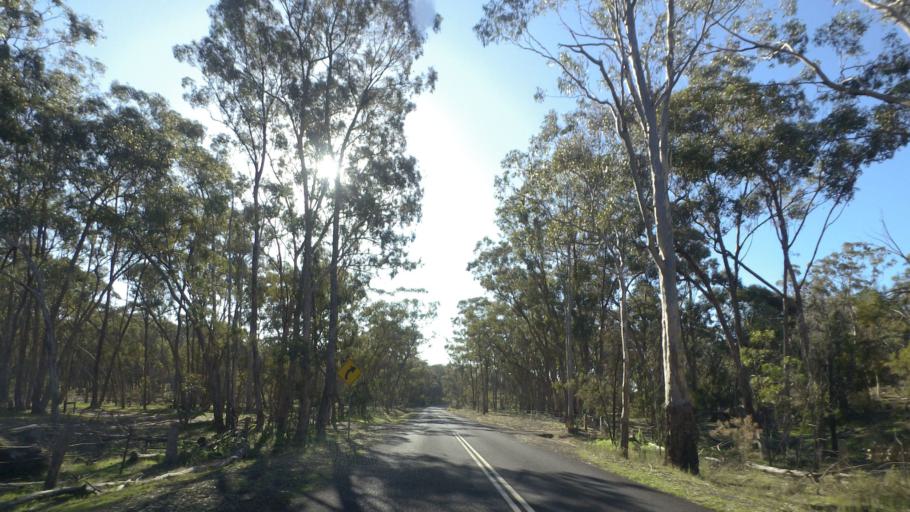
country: AU
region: Victoria
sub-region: Greater Bendigo
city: Kangaroo Flat
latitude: -36.8813
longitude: 144.2816
